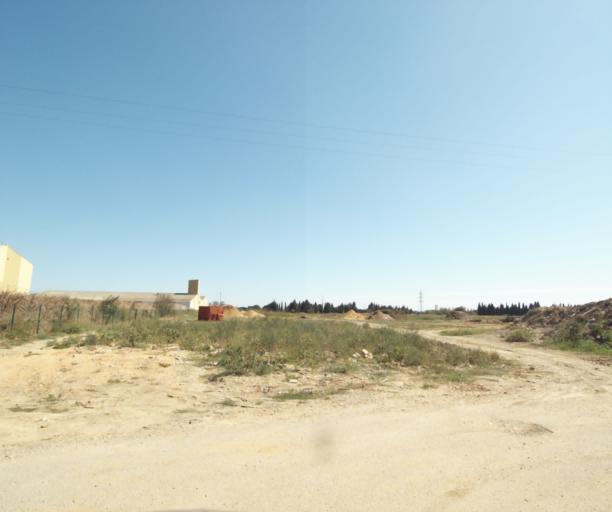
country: FR
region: Languedoc-Roussillon
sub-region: Departement du Gard
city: Rodilhan
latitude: 43.8145
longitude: 4.4226
